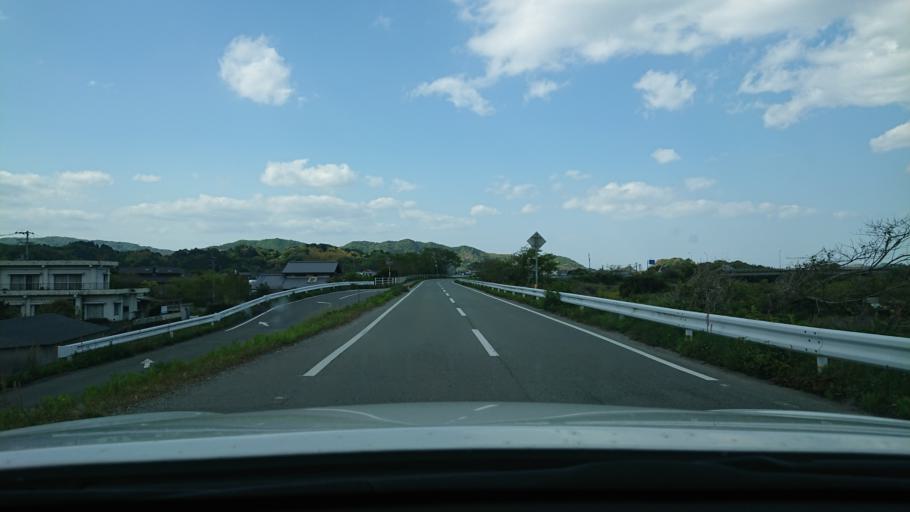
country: JP
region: Tokushima
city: Komatsushimacho
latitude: 33.9922
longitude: 134.5464
